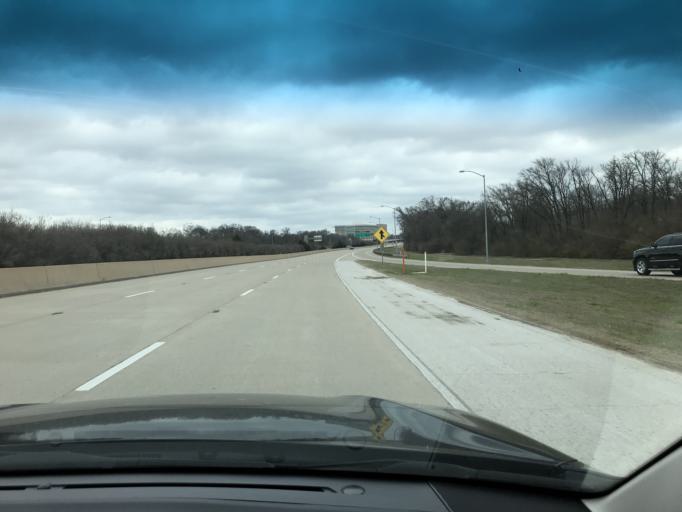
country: US
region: Texas
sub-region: Tarrant County
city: Westworth
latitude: 32.7005
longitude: -97.4058
